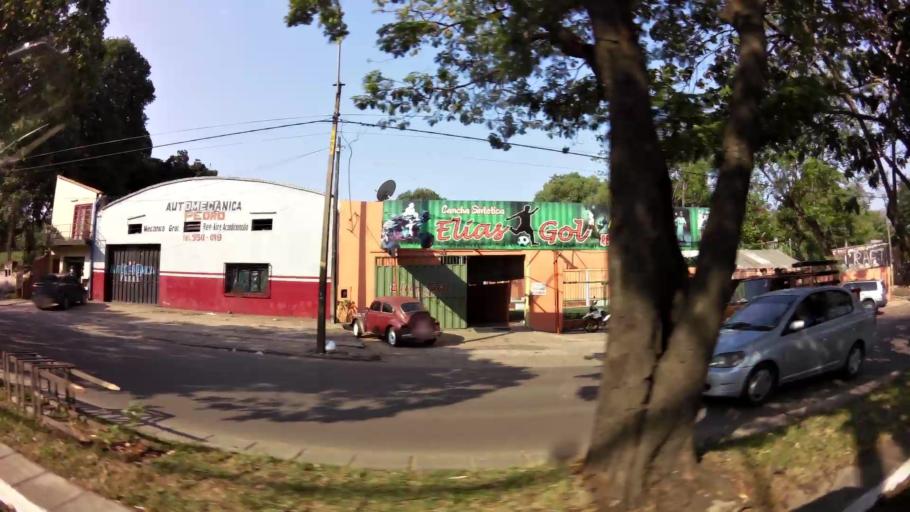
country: PY
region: Asuncion
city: Asuncion
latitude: -25.3152
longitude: -57.6094
